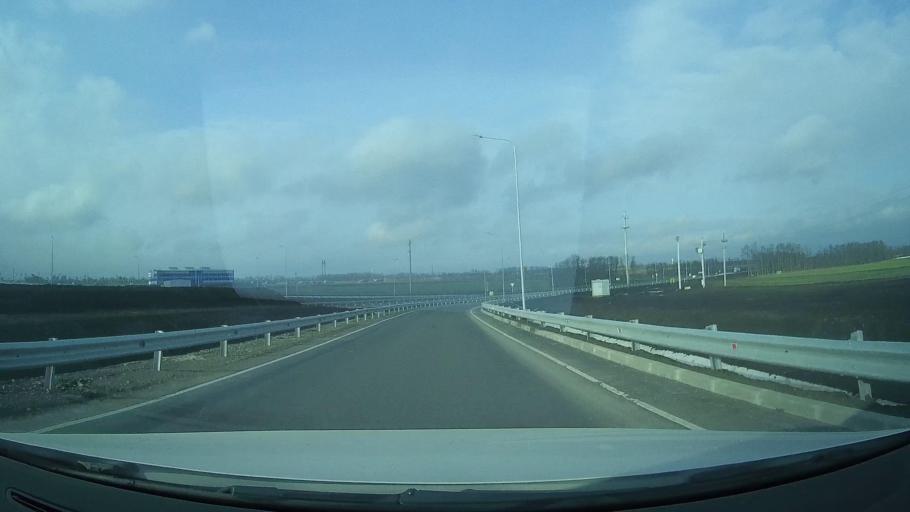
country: RU
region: Rostov
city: Grushevskaya
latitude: 47.3797
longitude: 39.8469
